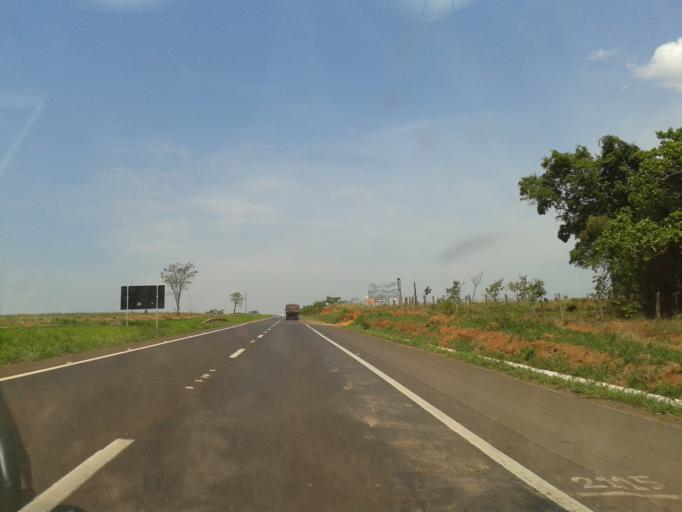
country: BR
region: Minas Gerais
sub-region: Monte Alegre De Minas
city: Monte Alegre de Minas
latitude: -18.8879
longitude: -48.7183
